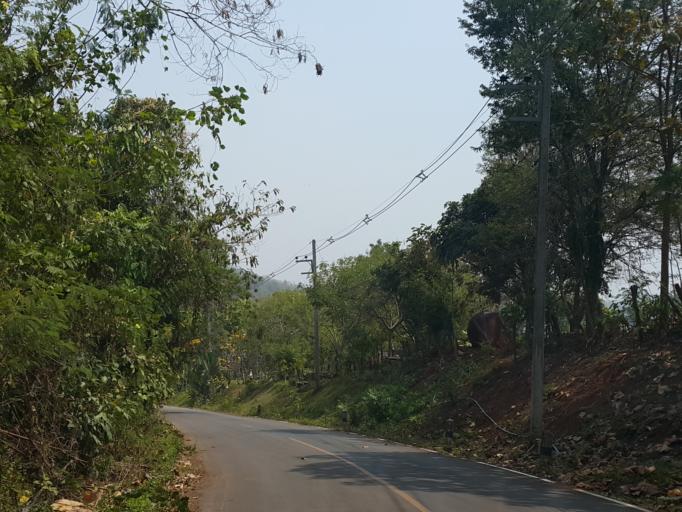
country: TH
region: Lampang
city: Mueang Pan
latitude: 18.8202
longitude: 99.4506
